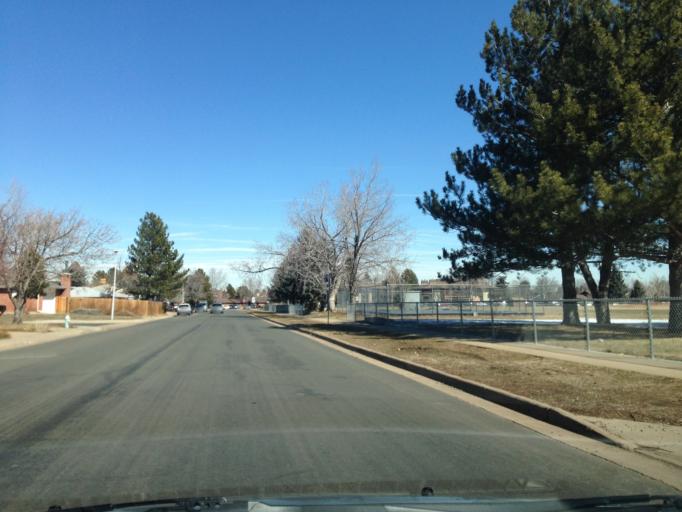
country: US
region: Colorado
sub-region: Boulder County
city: Boulder
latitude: 39.9946
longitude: -105.2299
